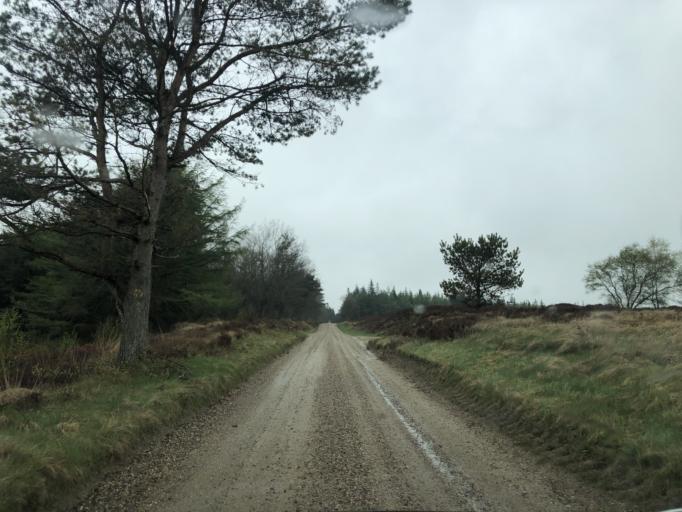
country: DK
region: Central Jutland
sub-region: Lemvig Kommune
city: Lemvig
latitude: 56.4746
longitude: 8.3783
